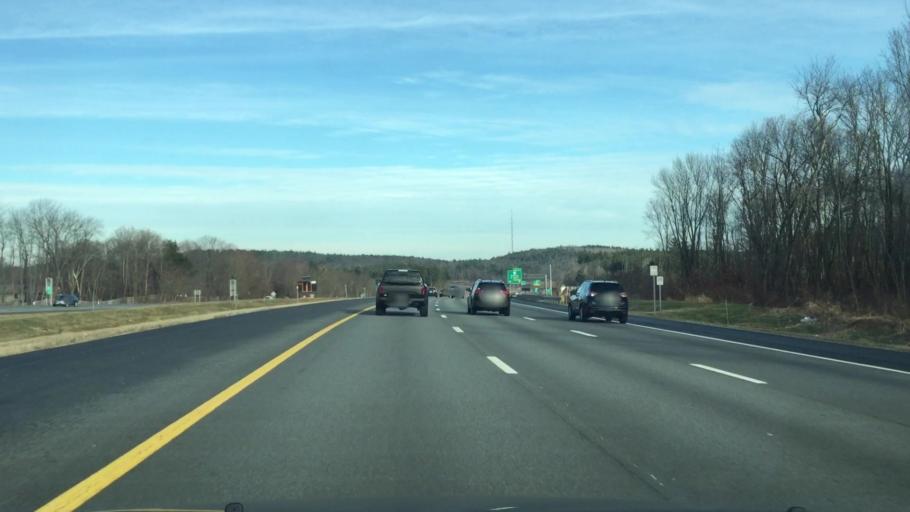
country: US
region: New Hampshire
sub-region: Rockingham County
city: Windham
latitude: 42.7952
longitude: -71.2717
